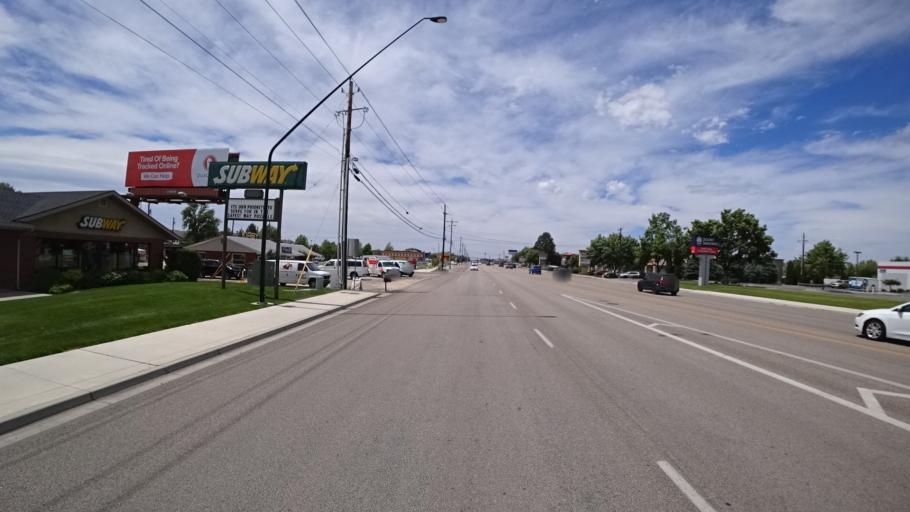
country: US
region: Idaho
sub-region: Ada County
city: Meridian
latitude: 43.6194
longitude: -116.3161
